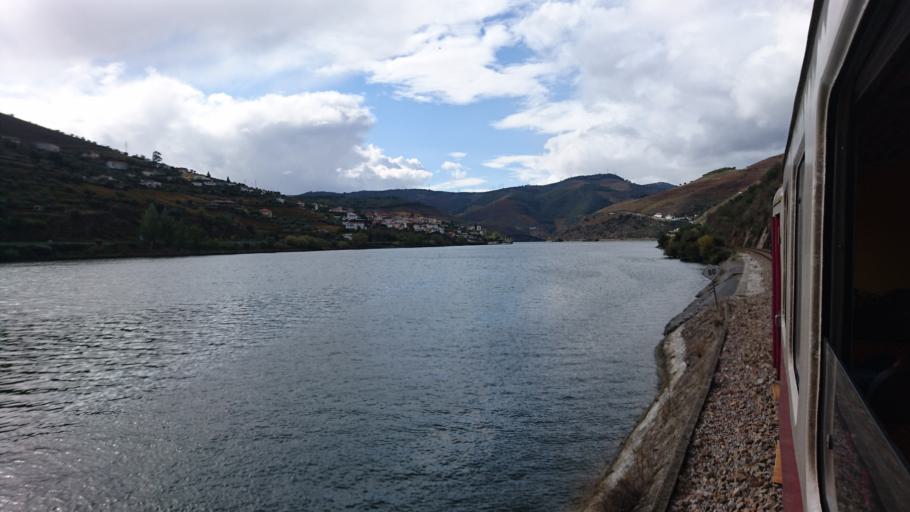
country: PT
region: Viseu
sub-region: Armamar
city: Armamar
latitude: 41.1586
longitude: -7.6745
